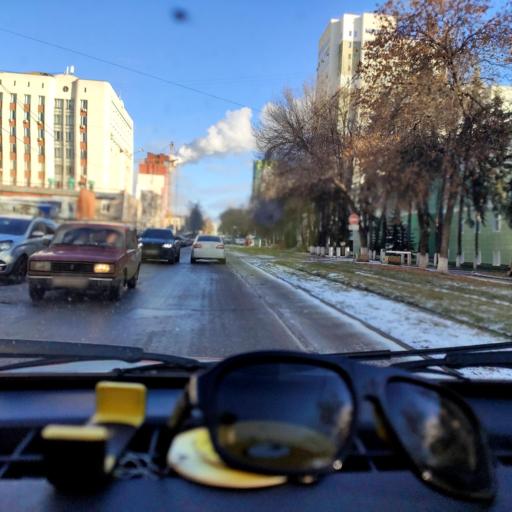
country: RU
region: Bashkortostan
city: Ufa
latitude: 54.7291
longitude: 55.9681
